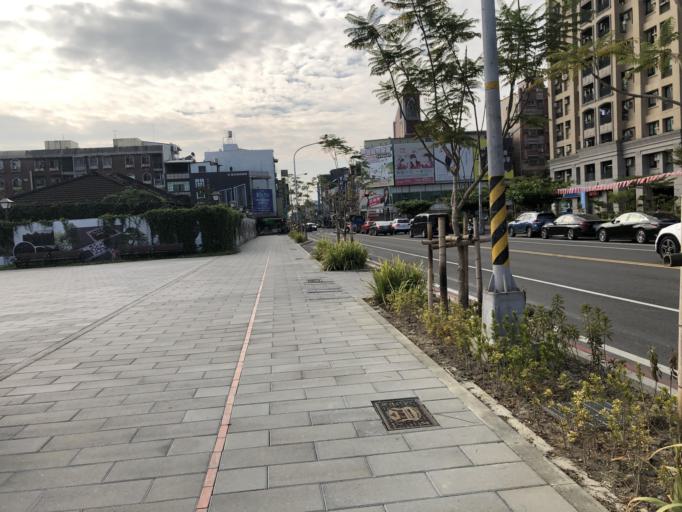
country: TW
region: Taiwan
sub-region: Pingtung
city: Pingtung
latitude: 22.6791
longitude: 120.4820
